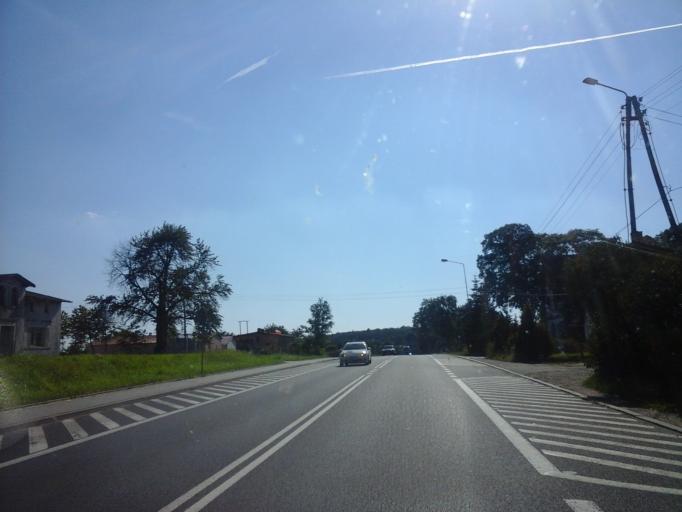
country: PL
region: West Pomeranian Voivodeship
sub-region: Powiat kolobrzeski
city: Ryman
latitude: 53.9632
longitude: 15.5811
